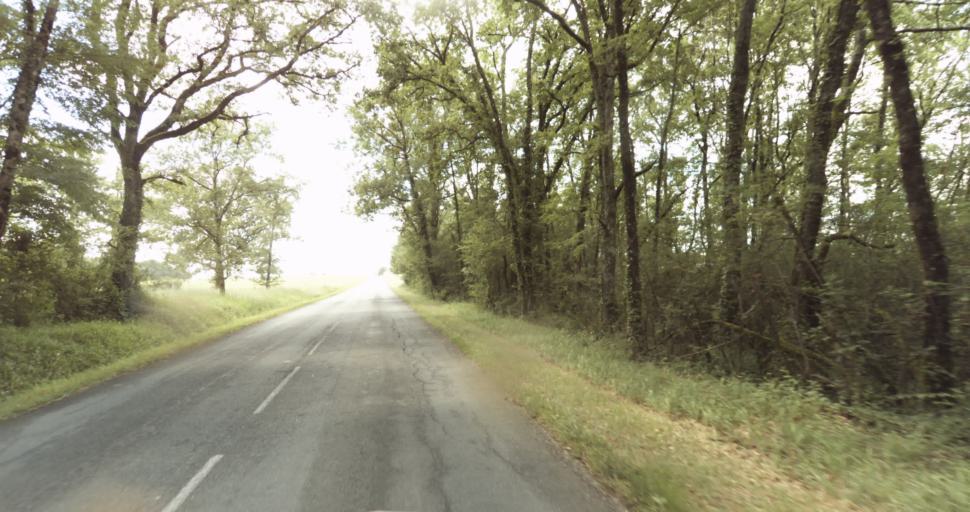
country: FR
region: Aquitaine
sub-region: Departement de la Dordogne
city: Beaumont-du-Perigord
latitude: 44.7122
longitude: 0.7503
